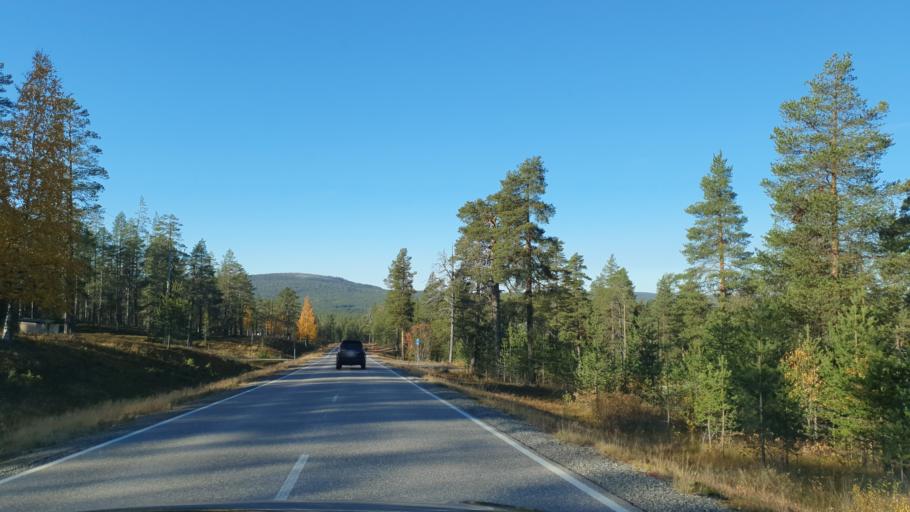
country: FI
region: Lapland
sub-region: Tunturi-Lappi
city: Kolari
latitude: 67.5936
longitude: 24.1952
